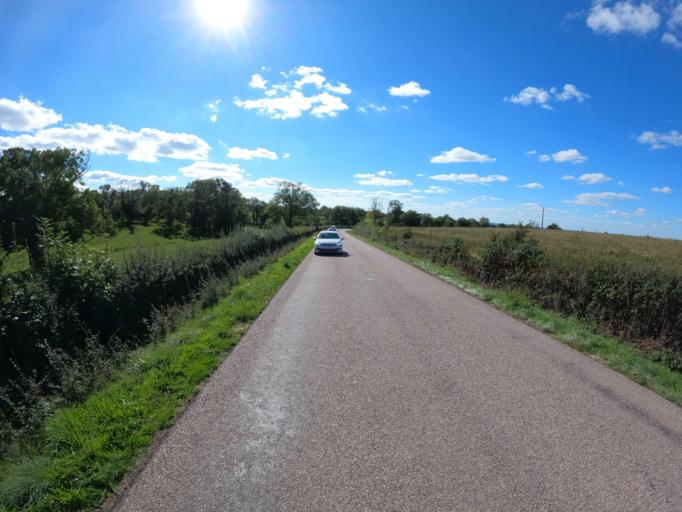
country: FR
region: Auvergne
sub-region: Departement de l'Allier
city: Buxieres-les-Mines
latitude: 46.4027
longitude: 2.9560
